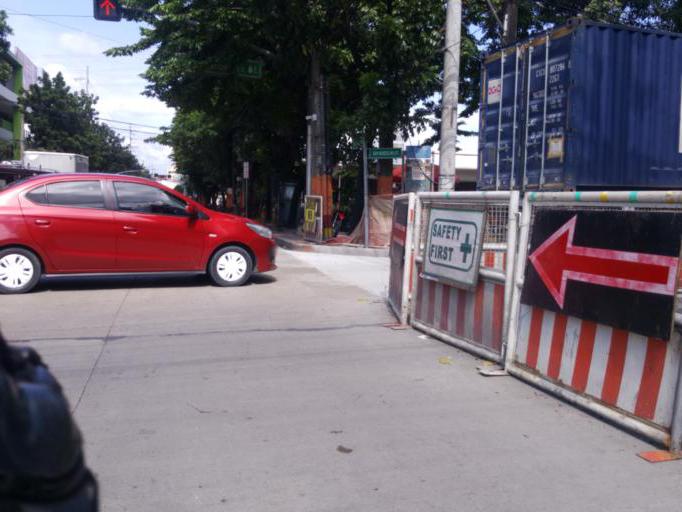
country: PH
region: Metro Manila
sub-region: City of Manila
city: Quiapo
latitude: 14.5831
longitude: 120.9869
